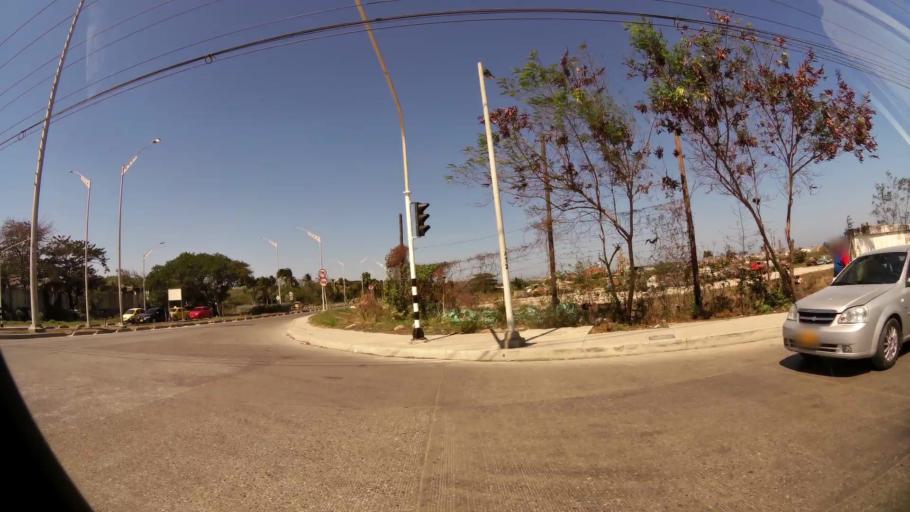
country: CO
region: Atlantico
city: Barranquilla
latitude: 10.9674
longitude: -74.7698
